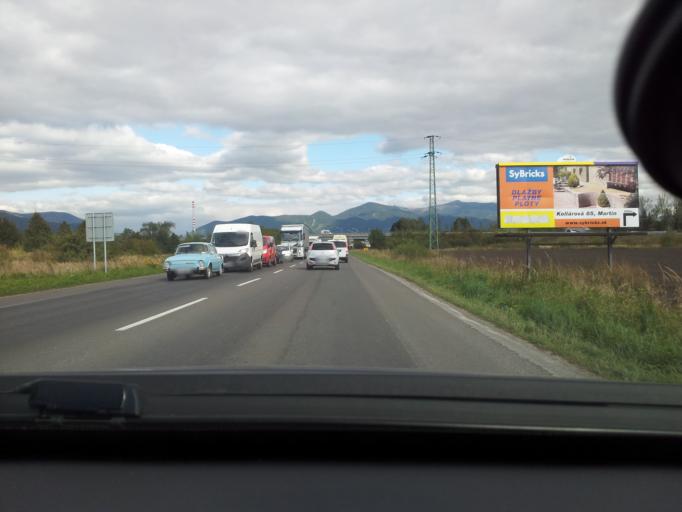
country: SK
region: Zilinsky
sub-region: Okres Martin
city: Martin
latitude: 49.0401
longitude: 18.9092
